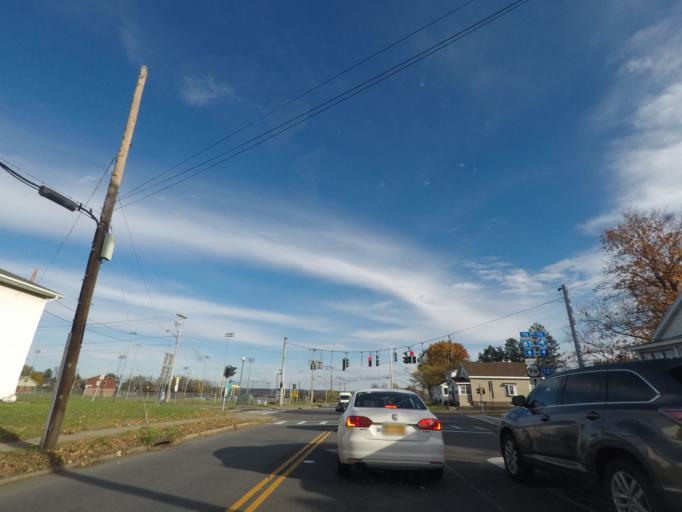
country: US
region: New York
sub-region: Albany County
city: Albany
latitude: 42.6360
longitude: -73.7782
